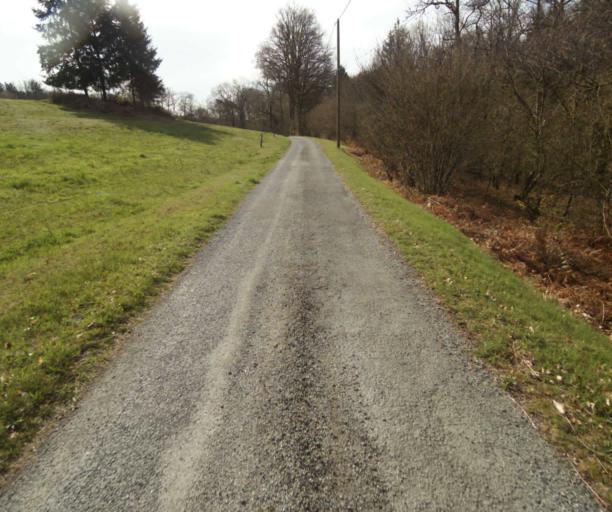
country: FR
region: Limousin
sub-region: Departement de la Correze
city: Correze
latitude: 45.3430
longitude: 1.8633
